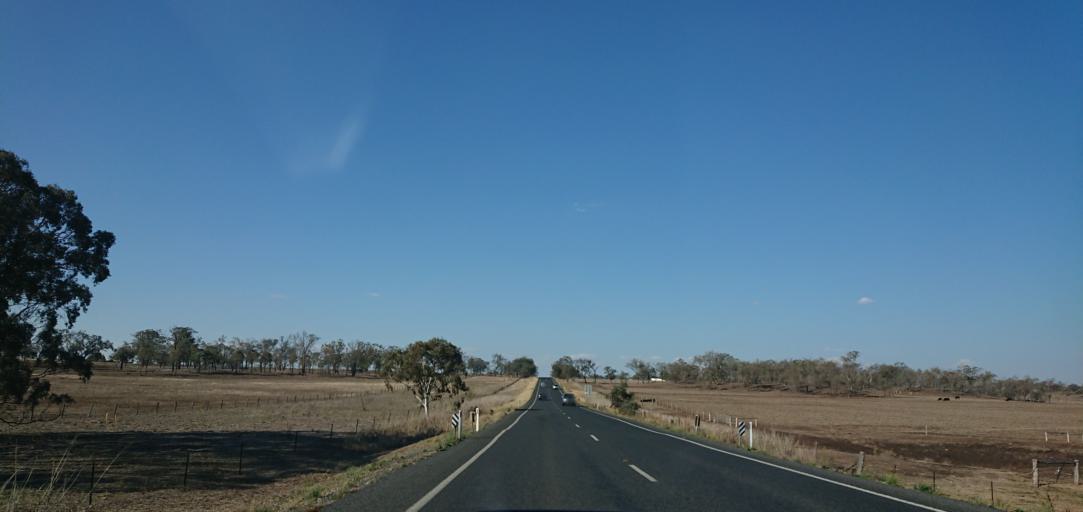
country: AU
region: Queensland
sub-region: Toowoomba
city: Westbrook
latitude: -27.6348
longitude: 151.7463
